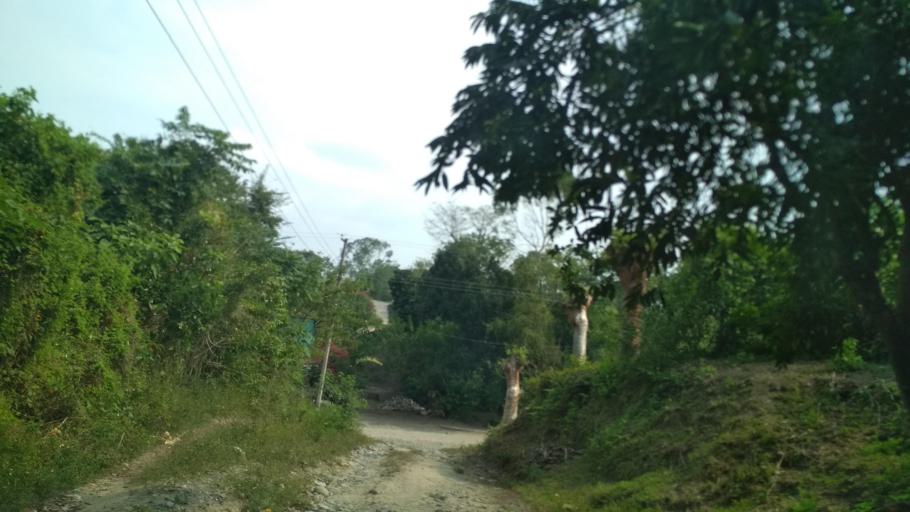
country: MM
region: Kayah
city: Loikaw
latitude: 20.2169
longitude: 97.2854
